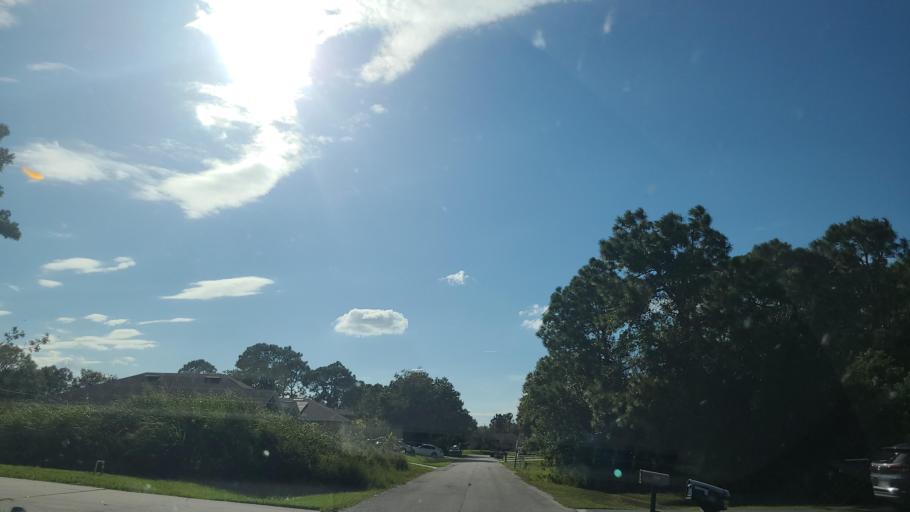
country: US
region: Florida
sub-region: Brevard County
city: West Melbourne
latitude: 27.9814
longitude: -80.6630
